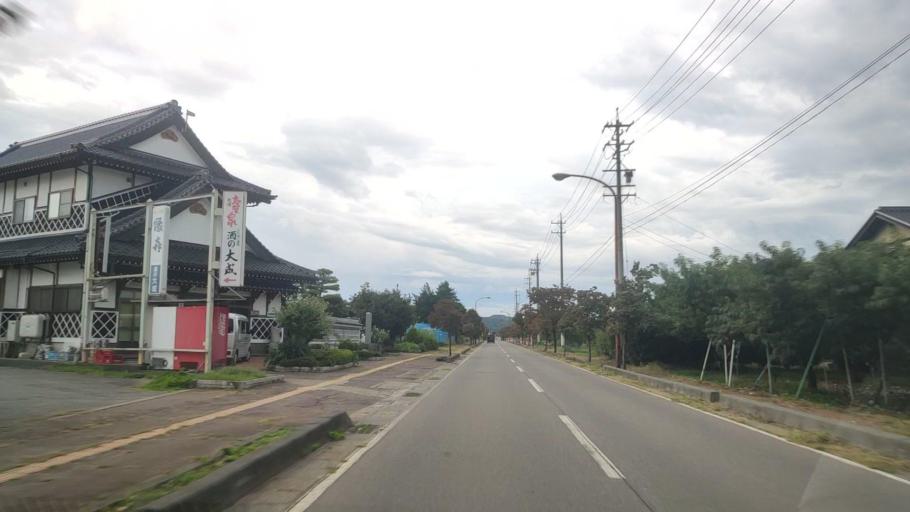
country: JP
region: Nagano
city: Nakano
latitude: 36.7819
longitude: 138.3558
